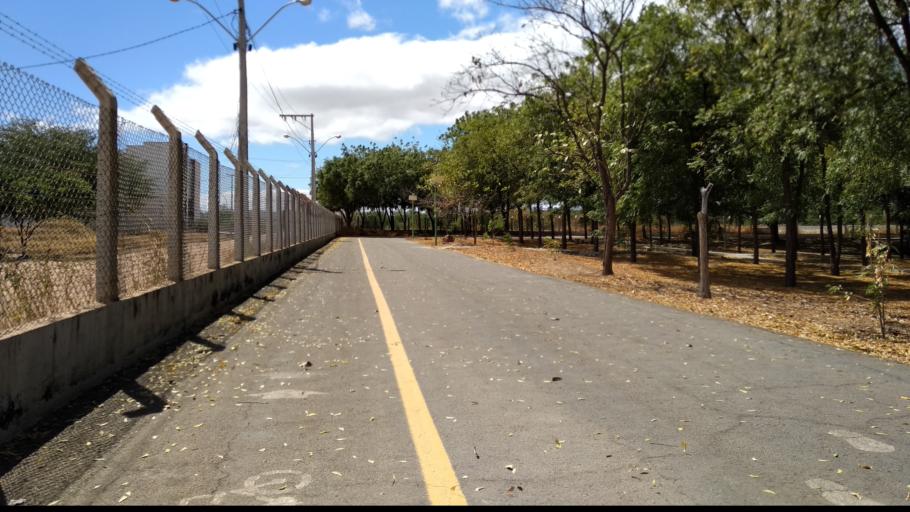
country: BR
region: Bahia
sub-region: Guanambi
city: Guanambi
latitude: -14.2234
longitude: -42.7634
